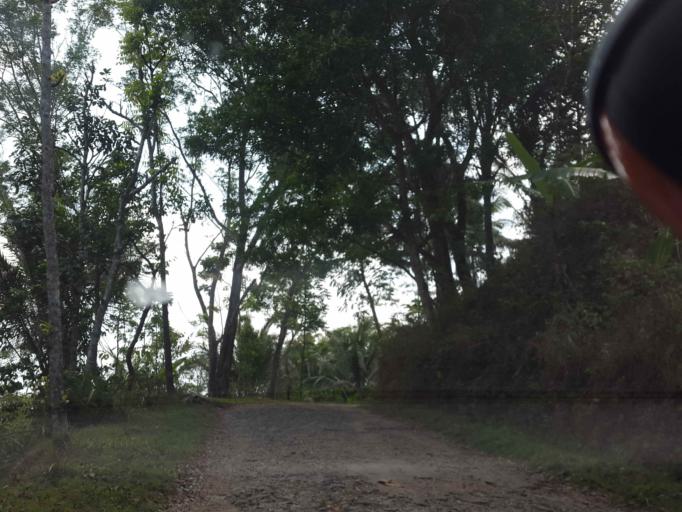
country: ID
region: East Java
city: Krajan
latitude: -8.2338
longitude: 111.1454
